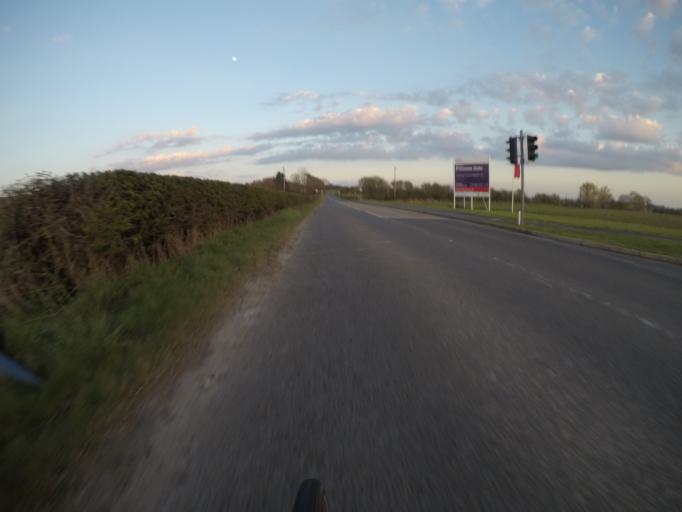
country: GB
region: Scotland
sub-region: South Ayrshire
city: Troon
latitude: 55.5579
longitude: -4.6283
